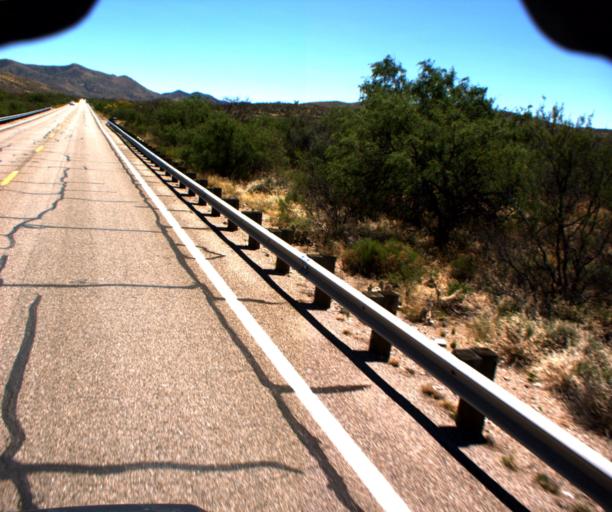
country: US
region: Arizona
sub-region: Pima County
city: Corona de Tucson
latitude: 31.9426
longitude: -110.6636
